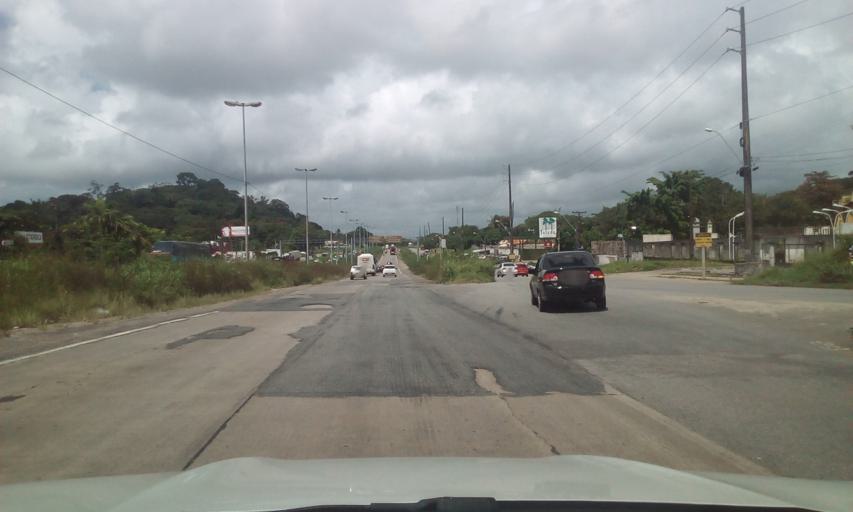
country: BR
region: Pernambuco
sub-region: Recife
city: Recife
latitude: -8.0113
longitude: -34.9379
